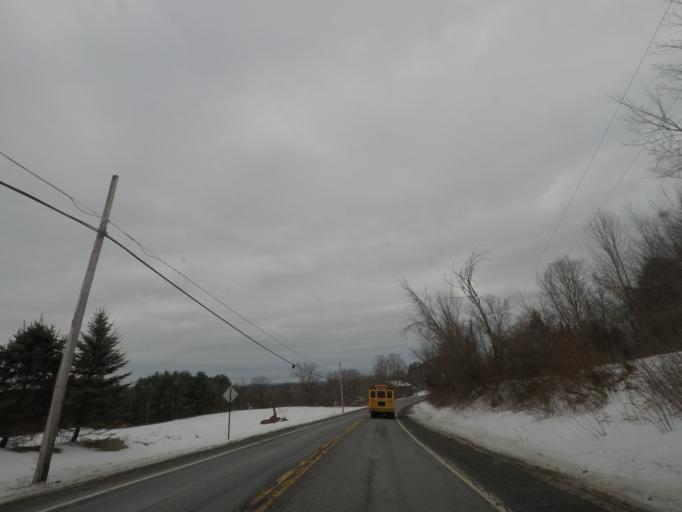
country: US
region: New York
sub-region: Saratoga County
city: Stillwater
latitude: 42.9519
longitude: -73.6660
